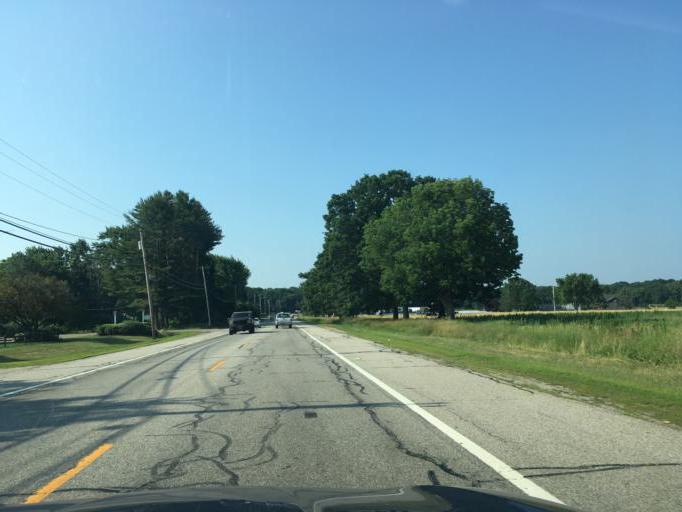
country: US
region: Rhode Island
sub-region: Washington County
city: Exeter
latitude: 41.5618
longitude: -71.5180
